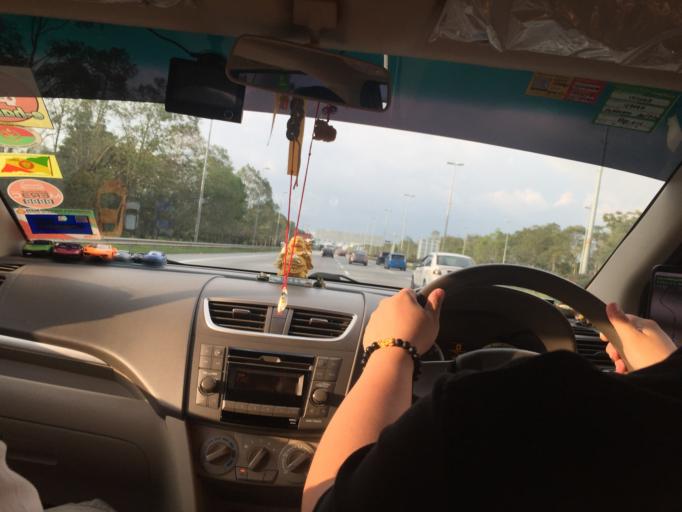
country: MY
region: Negeri Sembilan
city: Kampung Baharu Nilai
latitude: 2.7891
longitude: 101.6729
